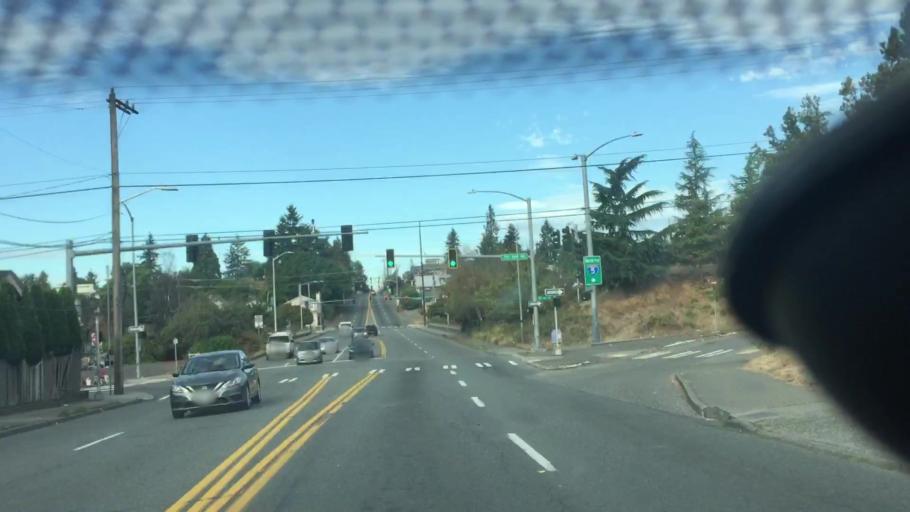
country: US
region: Washington
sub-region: King County
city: Seattle
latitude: 47.6643
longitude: -122.3190
